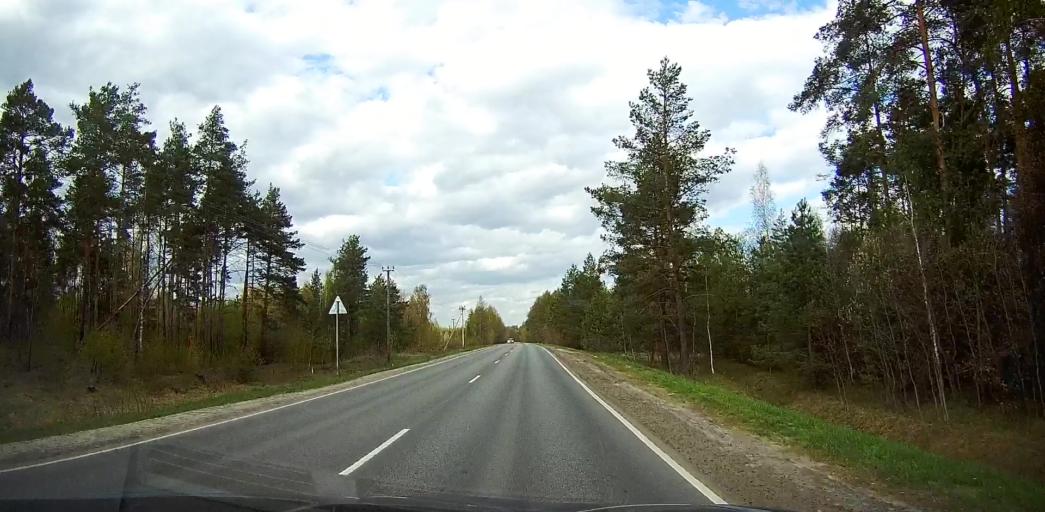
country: RU
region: Moskovskaya
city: Rakhmanovo
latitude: 55.7295
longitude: 38.6307
